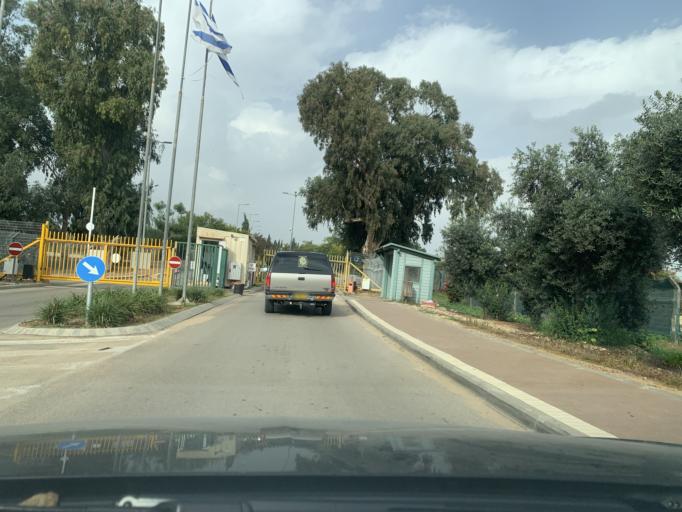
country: IL
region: Central District
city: Tirah
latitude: 32.2200
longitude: 34.9393
